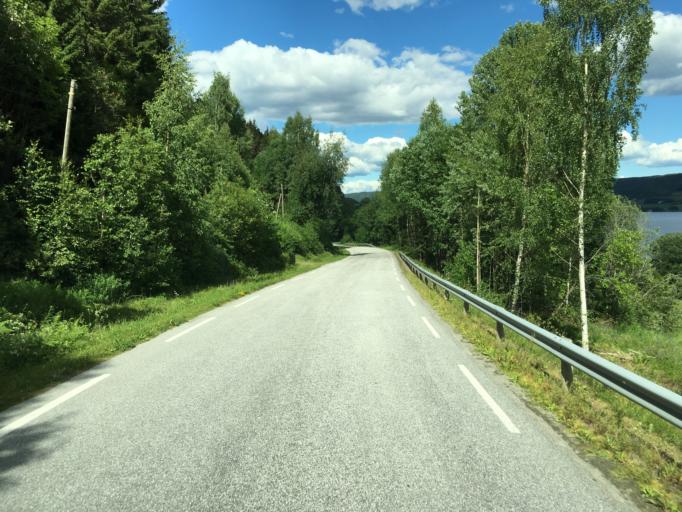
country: NO
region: Oppland
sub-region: Sondre Land
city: Hov
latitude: 60.5755
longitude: 10.2895
